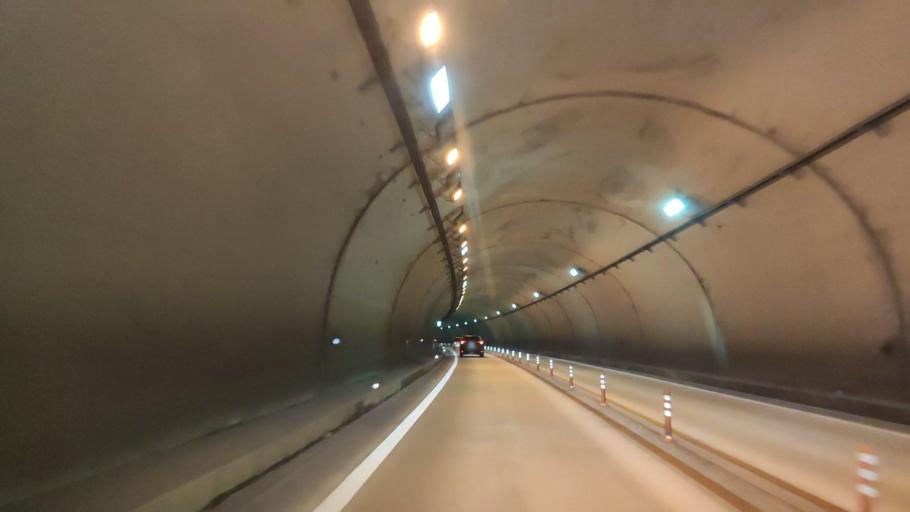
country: JP
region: Hiroshima
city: Innoshima
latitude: 34.2930
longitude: 133.1433
